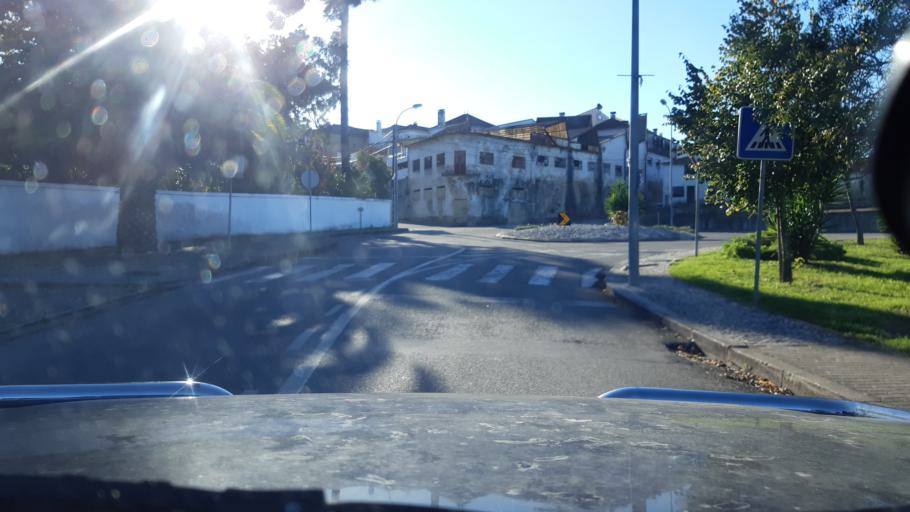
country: PT
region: Aveiro
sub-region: Agueda
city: Agueda
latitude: 40.5606
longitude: -8.4400
